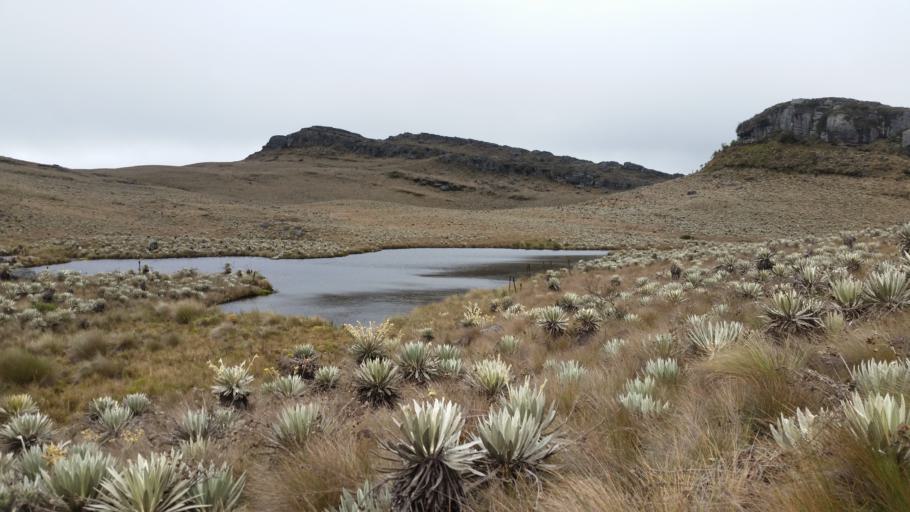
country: CO
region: Cundinamarca
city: Pasca
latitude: 4.3687
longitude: -74.2142
